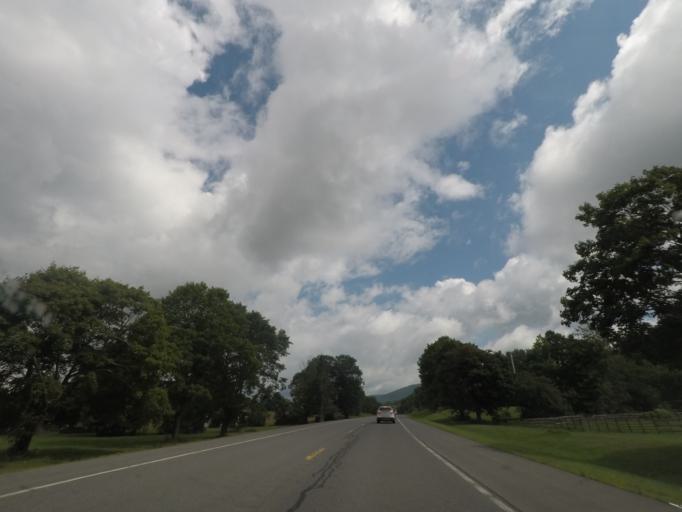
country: US
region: Massachusetts
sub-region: Berkshire County
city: Lanesborough
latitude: 42.5605
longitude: -73.3729
